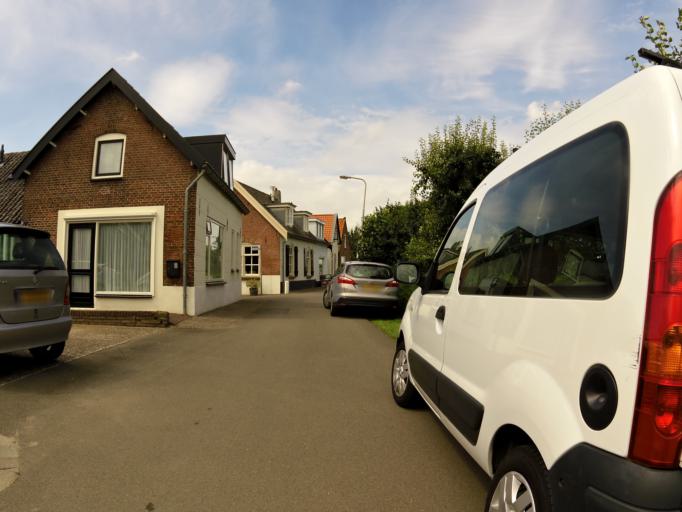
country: NL
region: South Holland
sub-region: Gemeente Leerdam
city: Leerdam
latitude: 51.8846
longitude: 5.1555
